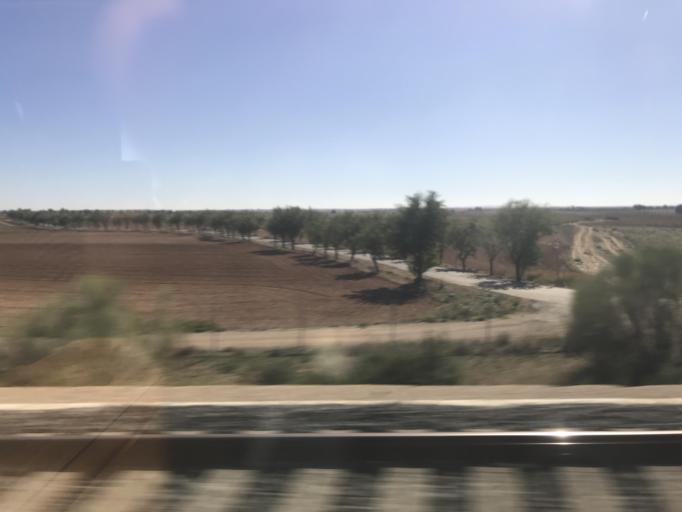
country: ES
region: Castille-La Mancha
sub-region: Province of Toledo
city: Villarrubia de Santiago
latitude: 39.9482
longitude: -3.4002
